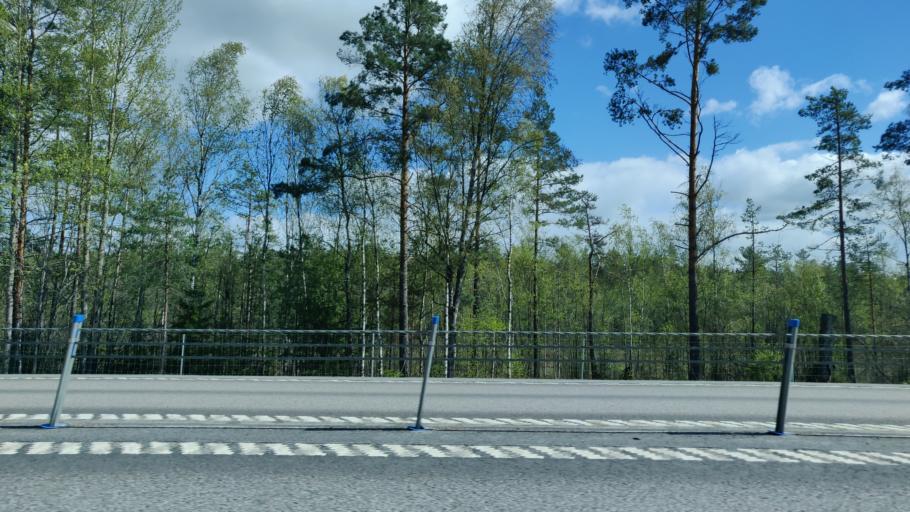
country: SE
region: Vaermland
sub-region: Karlstads Kommun
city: Karlstad
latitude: 59.4150
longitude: 13.5323
